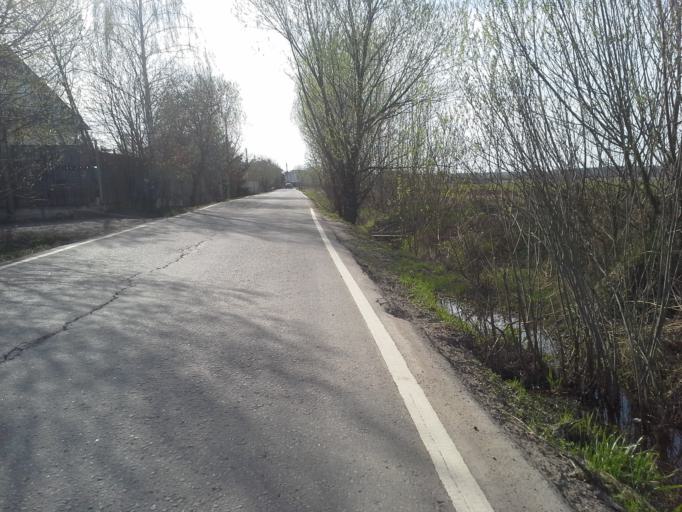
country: RU
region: Moskovskaya
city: Vatutinki
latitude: 55.4602
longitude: 37.3867
